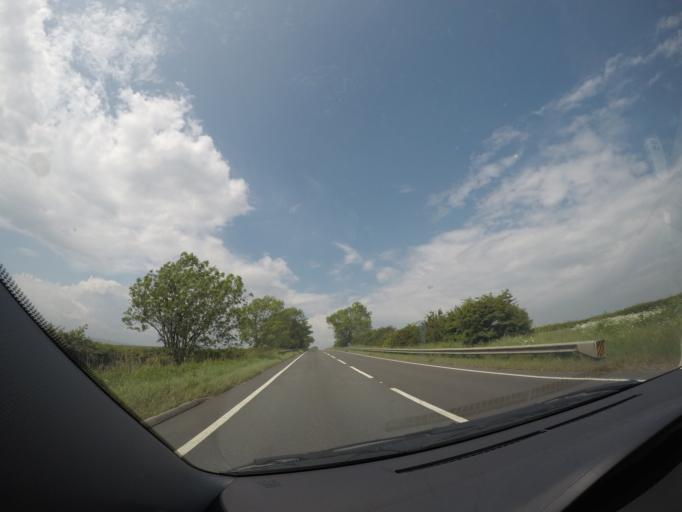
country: GB
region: England
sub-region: North Yorkshire
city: Catterick Garrison
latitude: 54.4556
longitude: -1.7110
